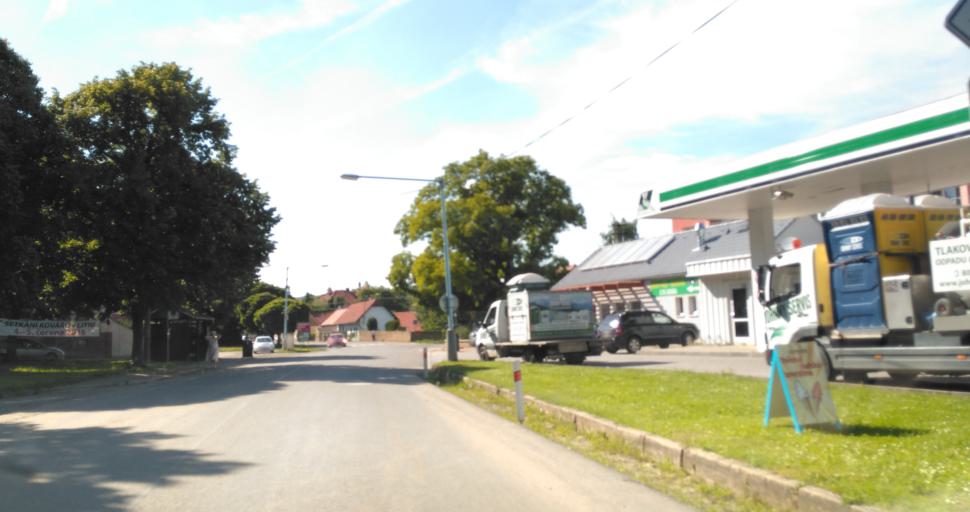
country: CZ
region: Central Bohemia
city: Revnice
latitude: 49.9028
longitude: 14.1535
